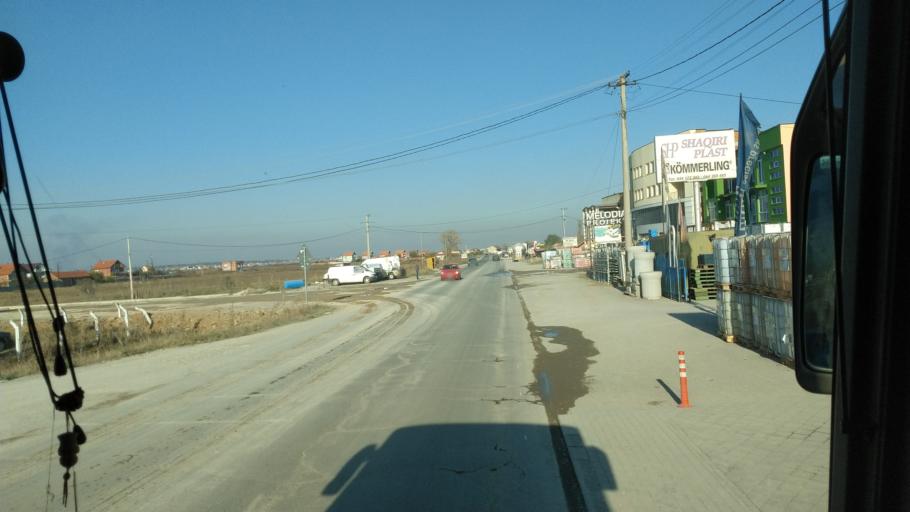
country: XK
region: Ferizaj
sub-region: Komuna e Shtimes
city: Shtime
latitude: 42.4454
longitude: 21.0595
